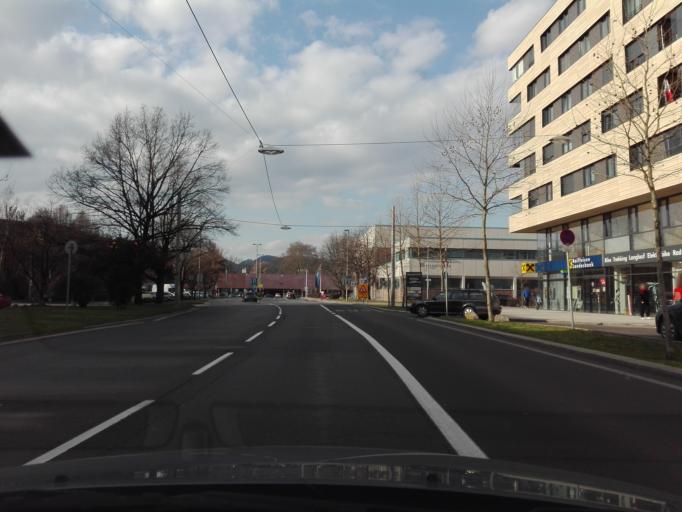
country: AT
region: Upper Austria
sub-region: Linz Stadt
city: Linz
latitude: 48.3101
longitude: 14.2986
